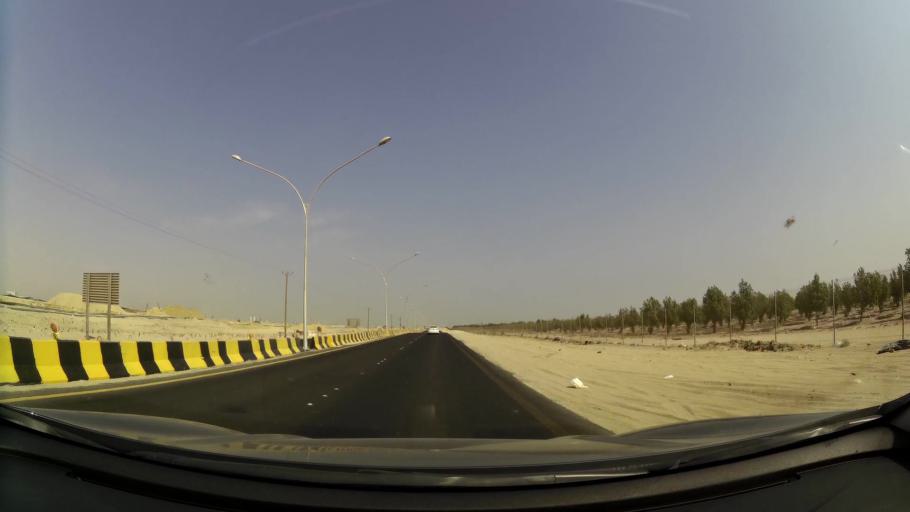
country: KW
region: Al Ahmadi
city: Al Fahahil
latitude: 28.9736
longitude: 48.1296
